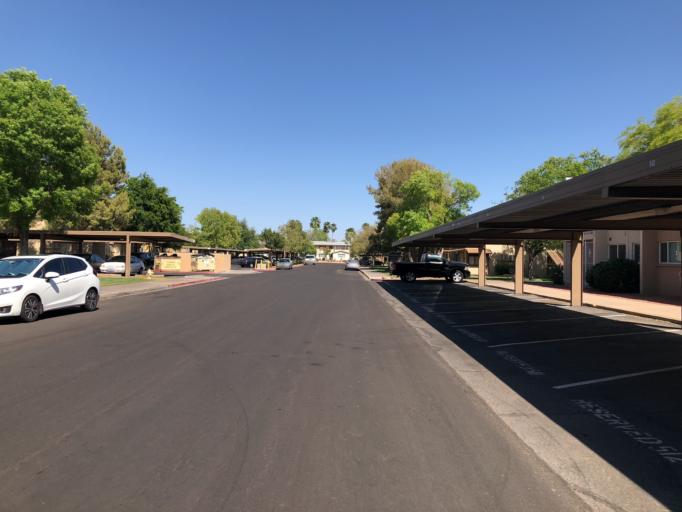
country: US
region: Arizona
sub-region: Maricopa County
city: Tempe
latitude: 33.4564
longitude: -111.9067
